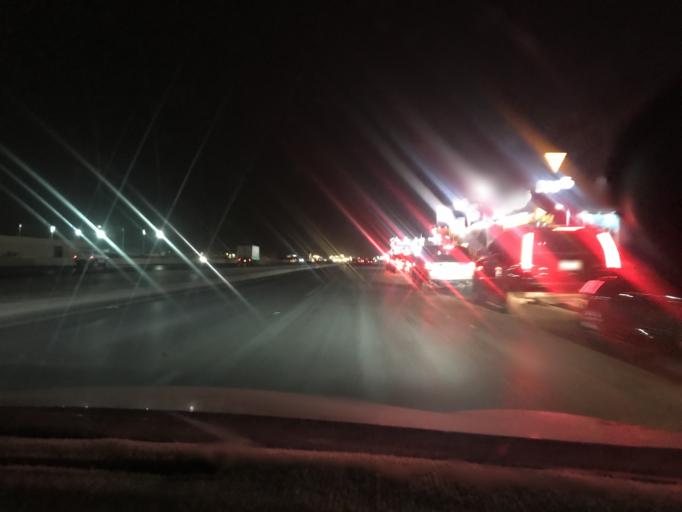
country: SA
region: Ar Riyad
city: Riyadh
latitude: 24.8462
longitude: 46.6045
